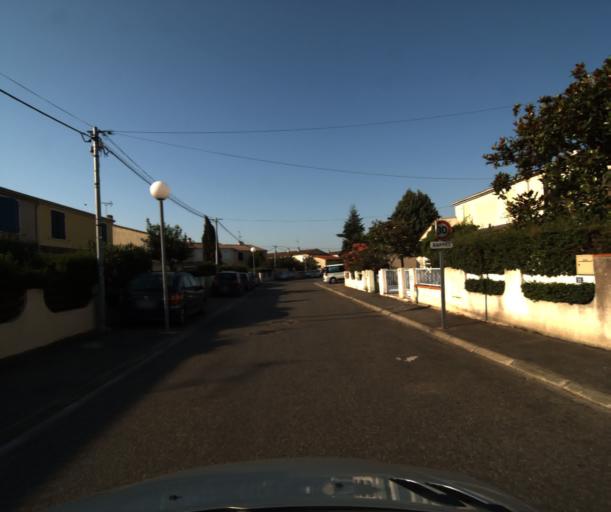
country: FR
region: Midi-Pyrenees
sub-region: Departement de la Haute-Garonne
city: Roquettes
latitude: 43.4812
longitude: 1.3881
